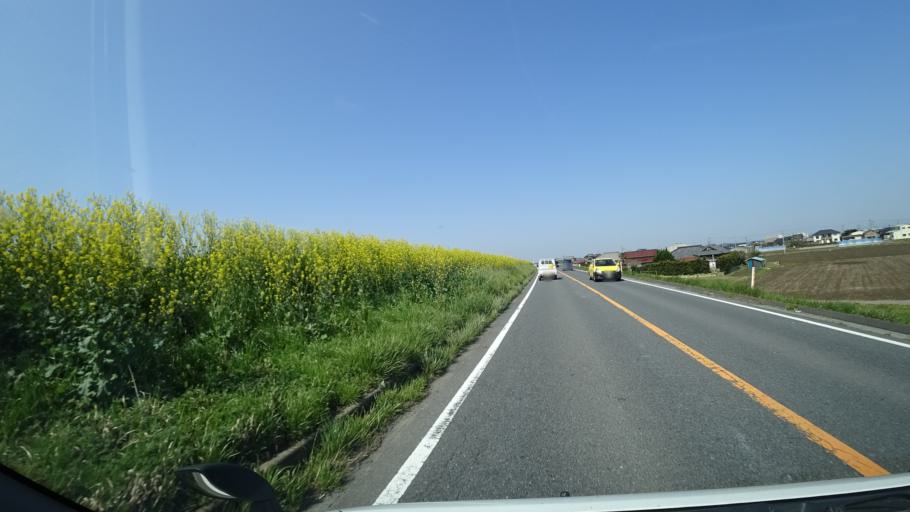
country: JP
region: Chiba
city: Katori-shi
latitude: 35.9200
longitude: 140.4667
